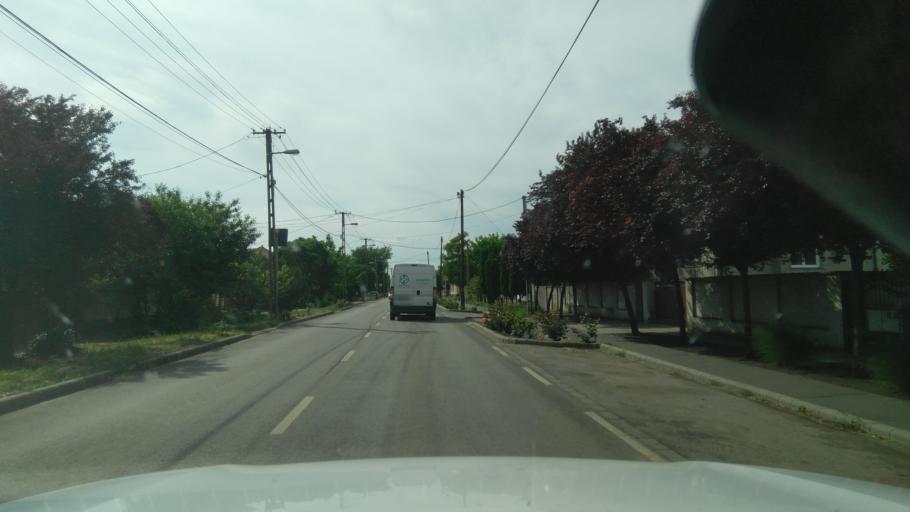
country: HU
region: Bekes
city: Medgyesegyhaza
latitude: 46.5011
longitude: 21.0219
